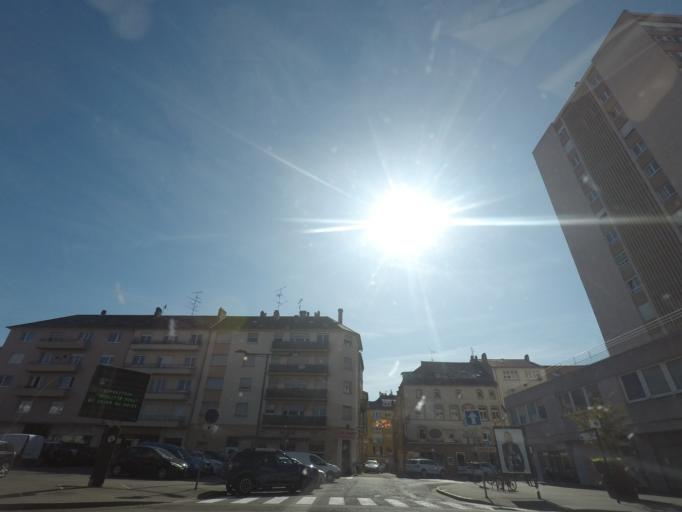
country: FR
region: Lorraine
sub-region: Departement de la Moselle
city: Thionville
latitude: 49.3592
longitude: 6.1655
